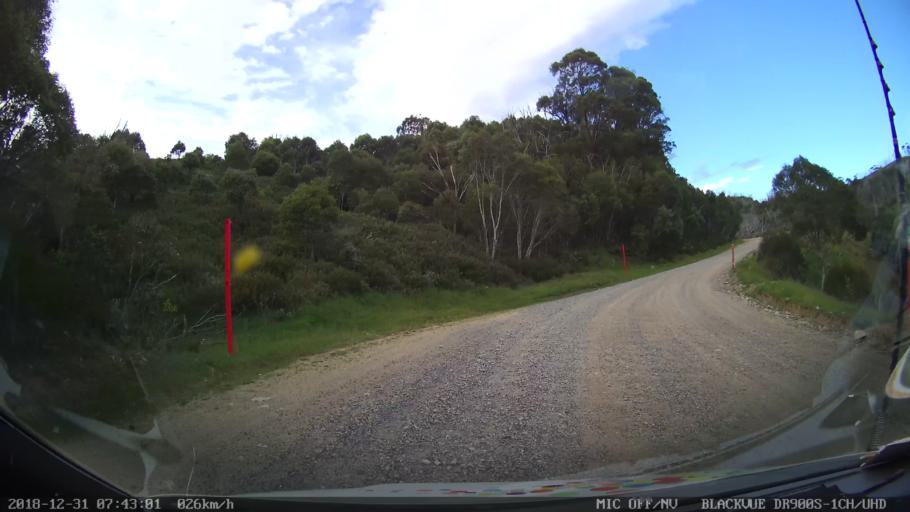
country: AU
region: New South Wales
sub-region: Snowy River
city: Jindabyne
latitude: -36.3591
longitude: 148.4075
